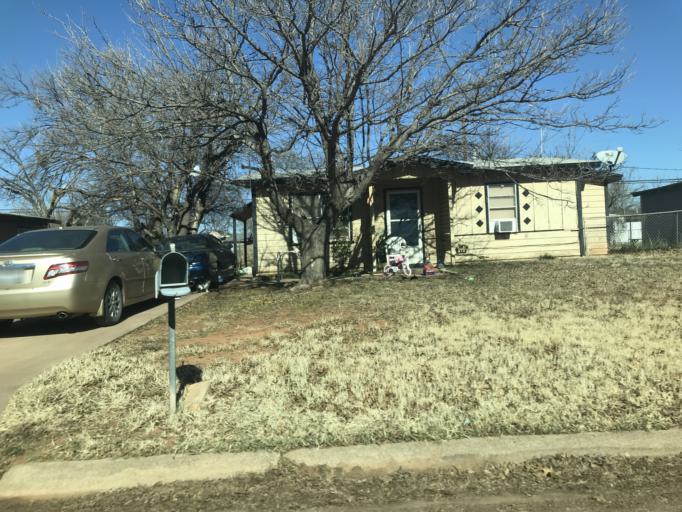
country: US
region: Texas
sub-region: Taylor County
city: Abilene
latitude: 32.4432
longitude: -99.7903
